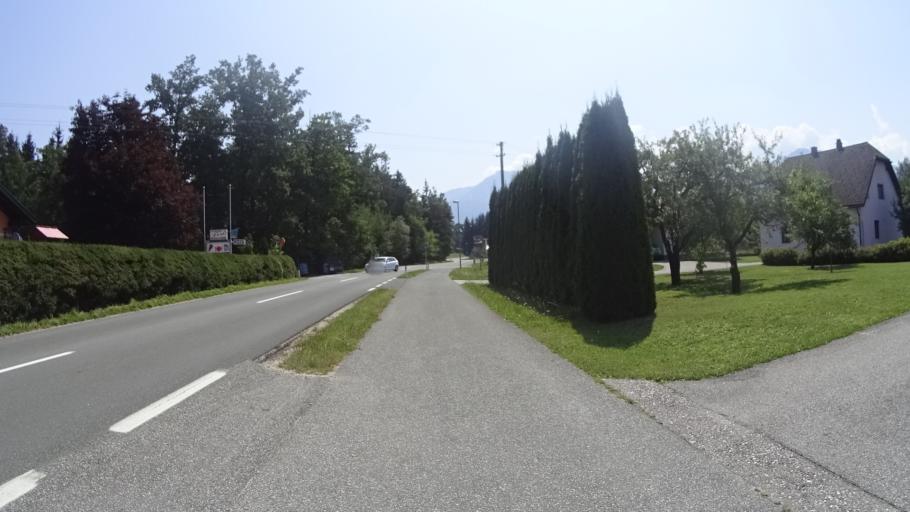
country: AT
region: Carinthia
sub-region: Politischer Bezirk Volkermarkt
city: Eberndorf
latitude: 46.5744
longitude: 14.6579
